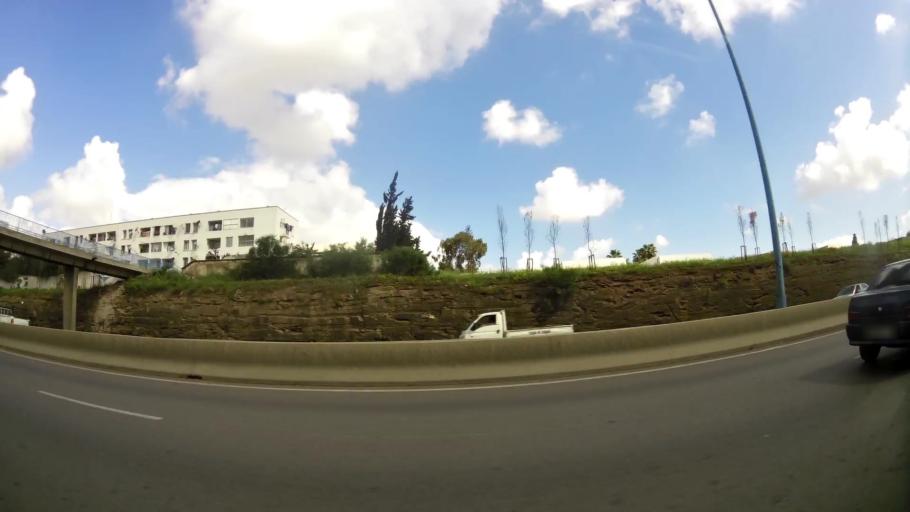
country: MA
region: Grand Casablanca
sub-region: Casablanca
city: Casablanca
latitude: 33.5555
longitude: -7.6127
